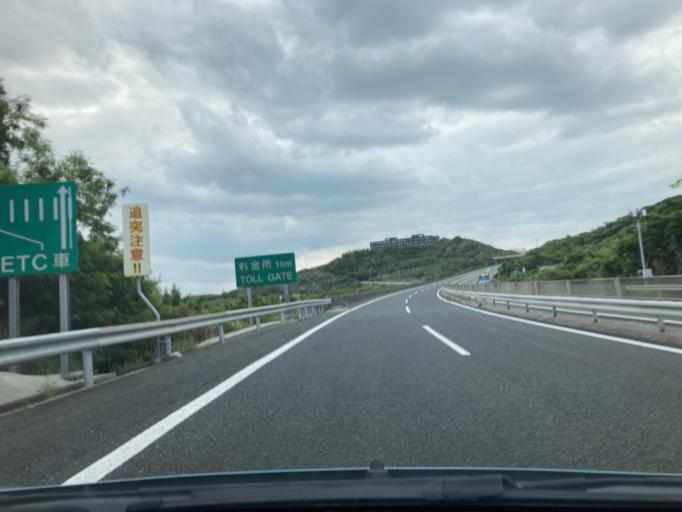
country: JP
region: Okinawa
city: Ginowan
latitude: 26.2147
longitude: 127.7376
